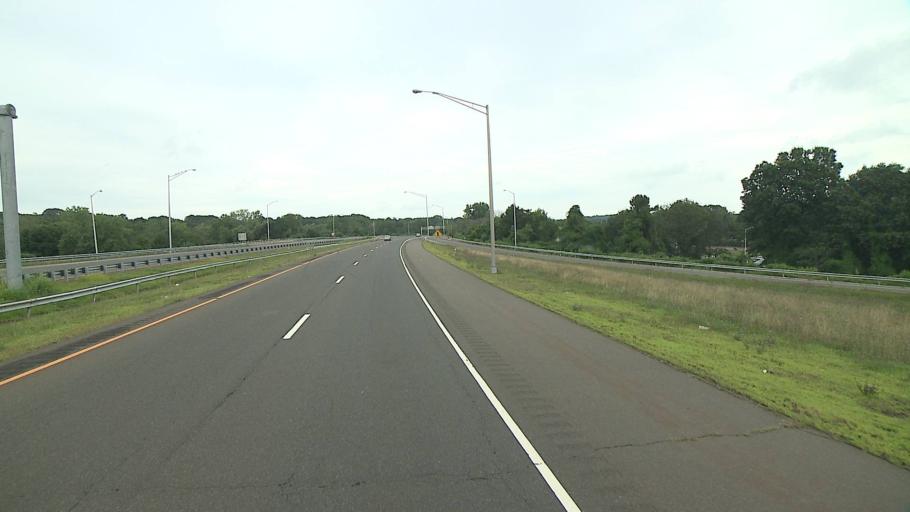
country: US
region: Connecticut
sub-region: New Haven County
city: Hamden
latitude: 41.3797
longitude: -72.8822
